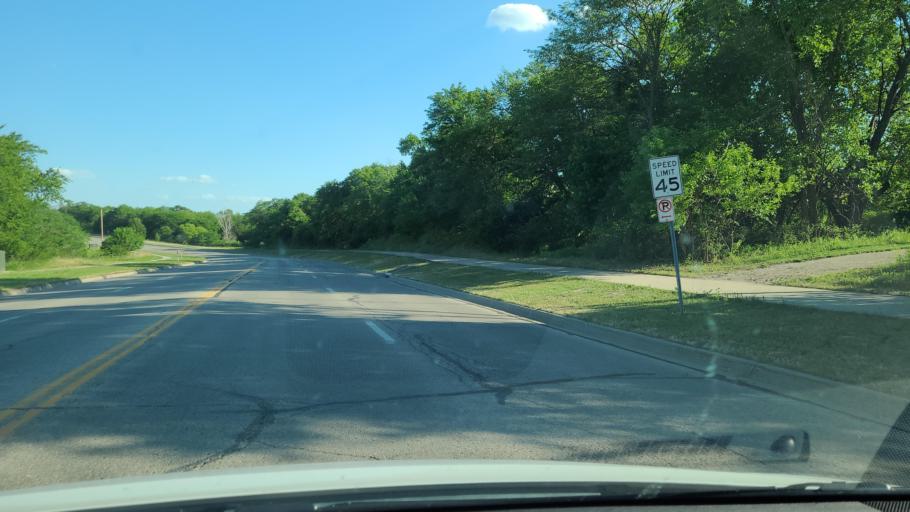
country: US
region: Kansas
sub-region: Douglas County
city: Lawrence
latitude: 38.9786
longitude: -95.3098
